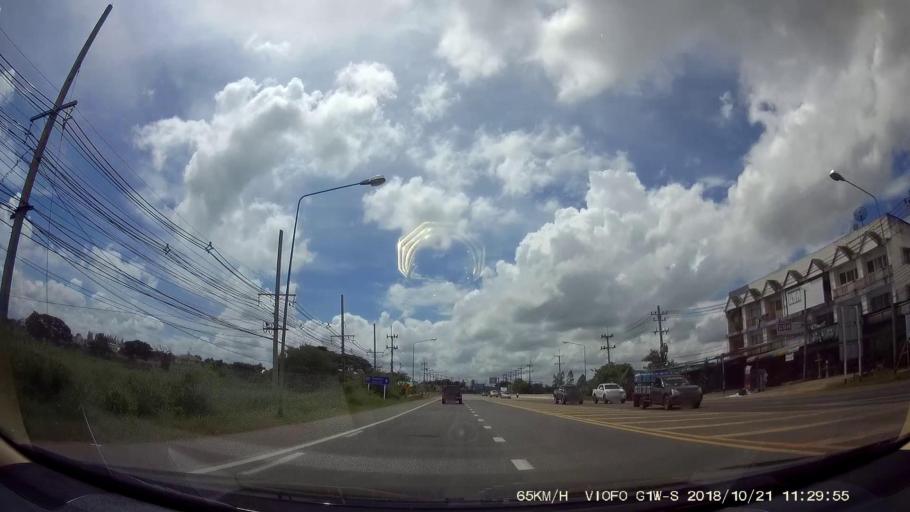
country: TH
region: Chaiyaphum
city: Chaiyaphum
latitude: 15.7845
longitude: 102.0276
